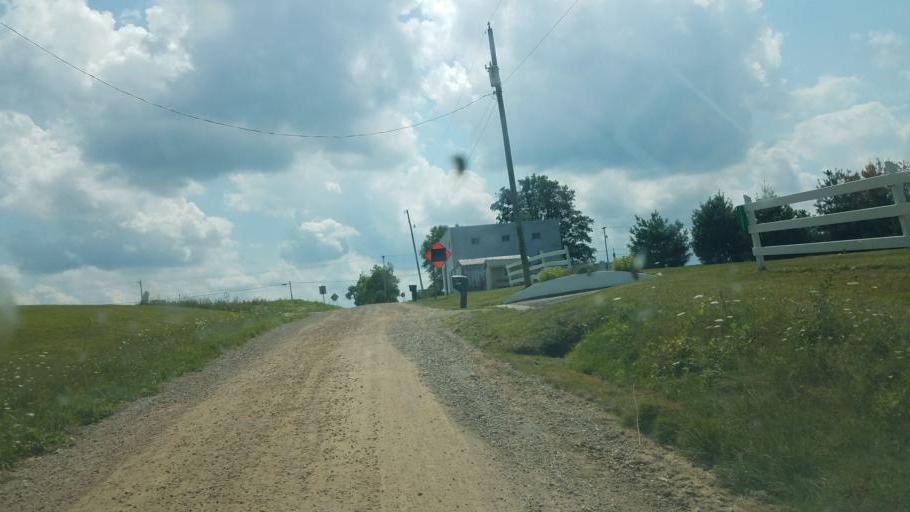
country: US
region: Ohio
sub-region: Knox County
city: Fredericktown
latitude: 40.4042
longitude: -82.5837
